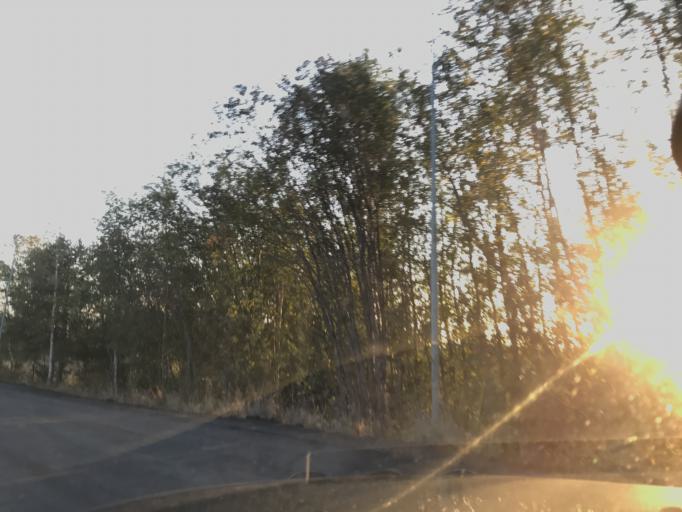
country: SE
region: Norrbotten
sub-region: Gallivare Kommun
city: Malmberget
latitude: 67.6385
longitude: 21.0172
